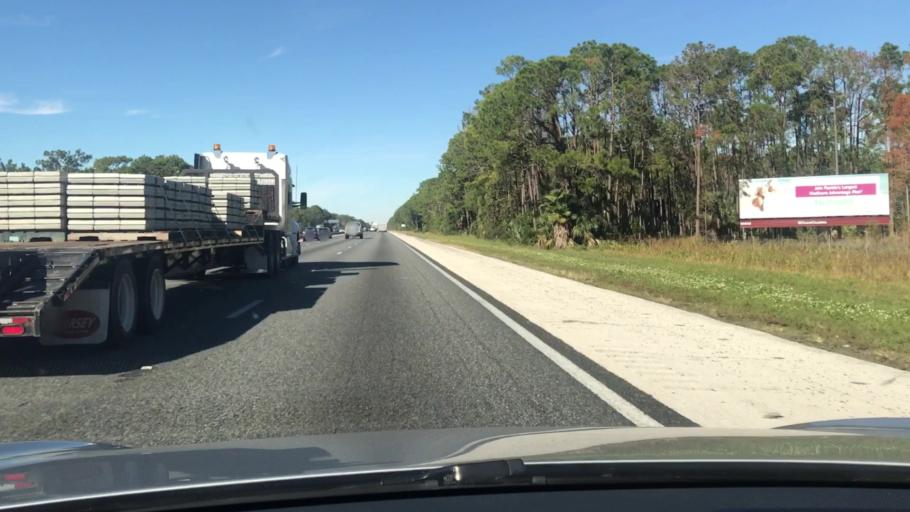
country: US
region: Florida
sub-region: Volusia County
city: Ormond-by-the-Sea
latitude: 29.3552
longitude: -81.1339
